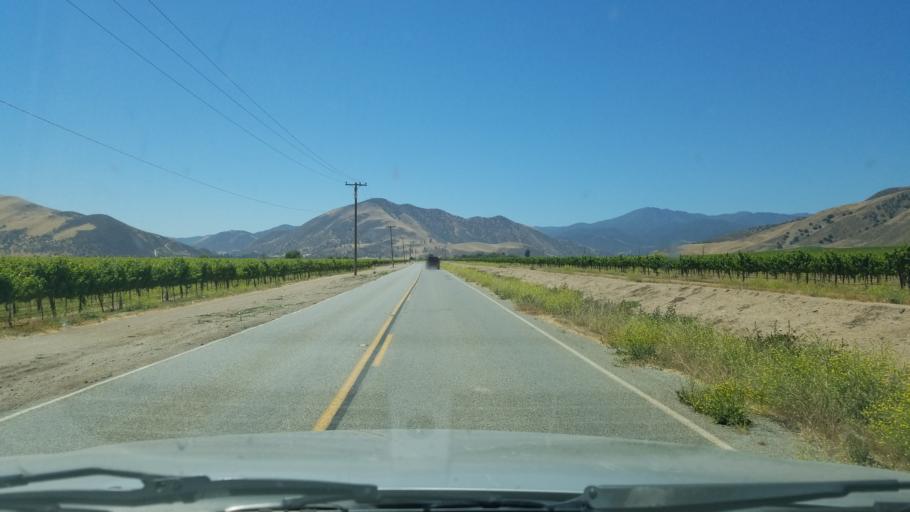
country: US
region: California
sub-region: Monterey County
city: Greenfield
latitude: 36.3137
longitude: -121.3113
